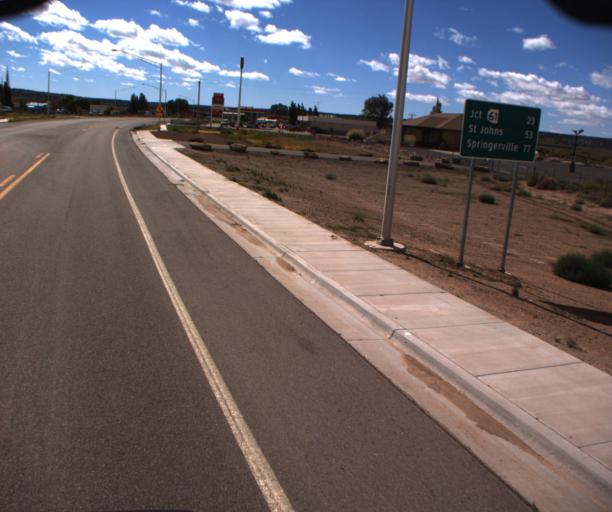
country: US
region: Arizona
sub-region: Apache County
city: Houck
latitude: 35.2114
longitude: -109.3311
